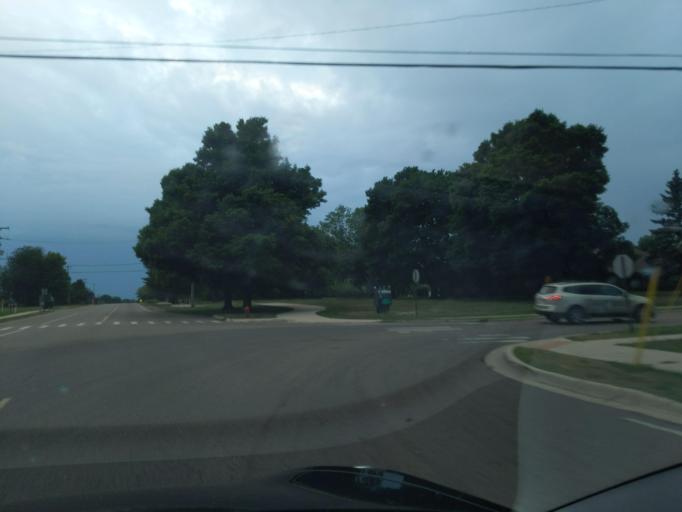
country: US
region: Michigan
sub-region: Clinton County
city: DeWitt
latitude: 42.8133
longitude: -84.5898
